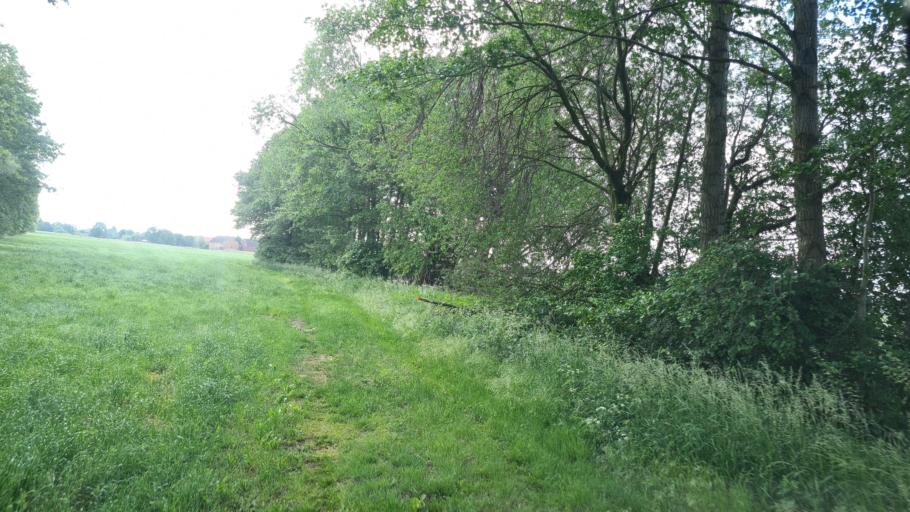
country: DE
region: Brandenburg
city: Sonnewalde
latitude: 51.6653
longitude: 13.6742
